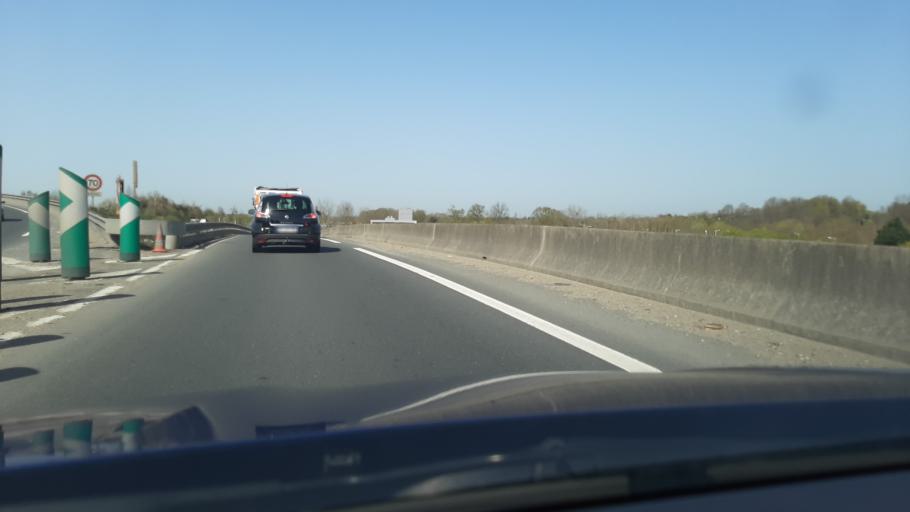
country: FR
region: Pays de la Loire
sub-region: Departement de Maine-et-Loire
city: Ecouflant
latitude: 47.5039
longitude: -0.5014
